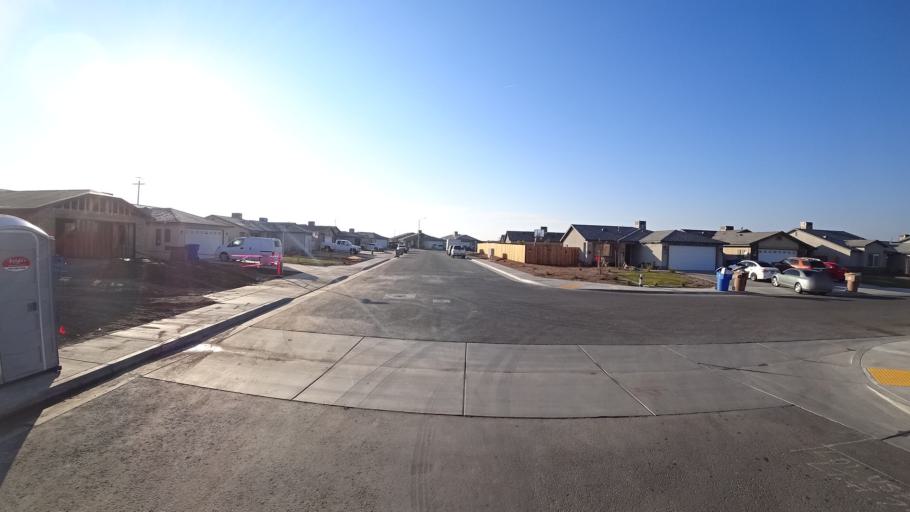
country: US
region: California
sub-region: Kern County
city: Greenfield
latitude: 35.2989
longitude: -118.9914
